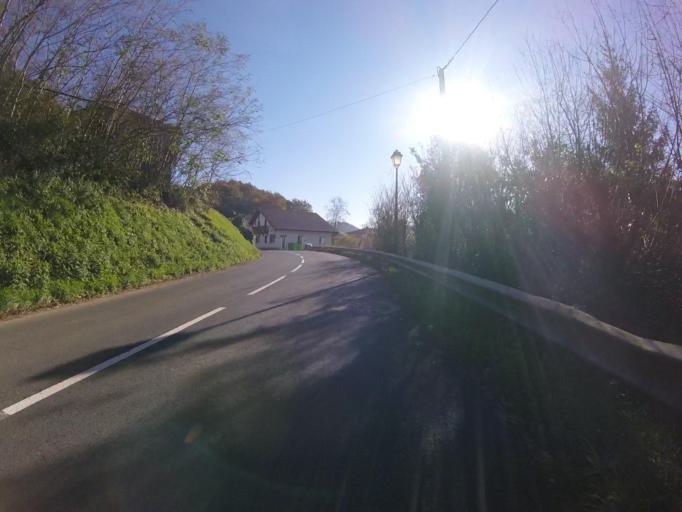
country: ES
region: Basque Country
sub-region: Provincia de Guipuzcoa
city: Irun
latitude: 43.3351
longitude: -1.7506
